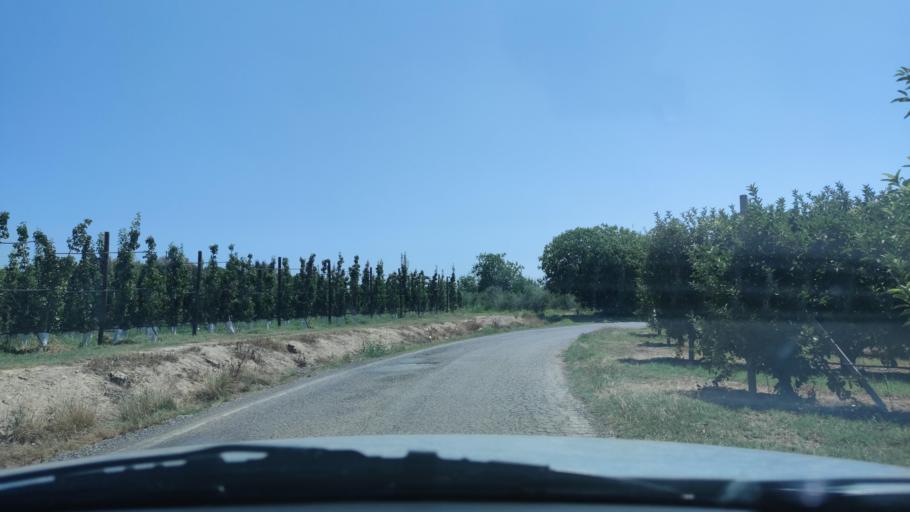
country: ES
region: Catalonia
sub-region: Provincia de Lleida
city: Torrefarrera
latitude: 41.6573
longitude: 0.5909
